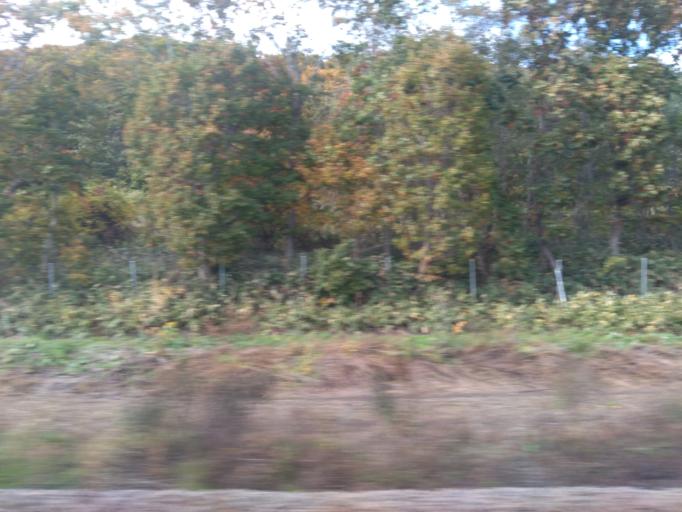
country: JP
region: Hokkaido
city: Shiraoi
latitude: 42.4626
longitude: 141.2113
